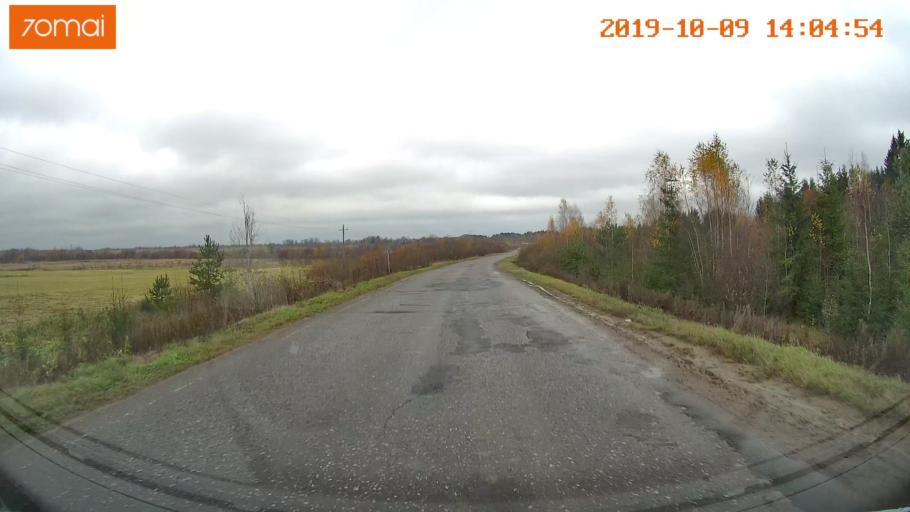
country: RU
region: Kostroma
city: Buy
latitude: 58.4586
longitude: 41.3885
